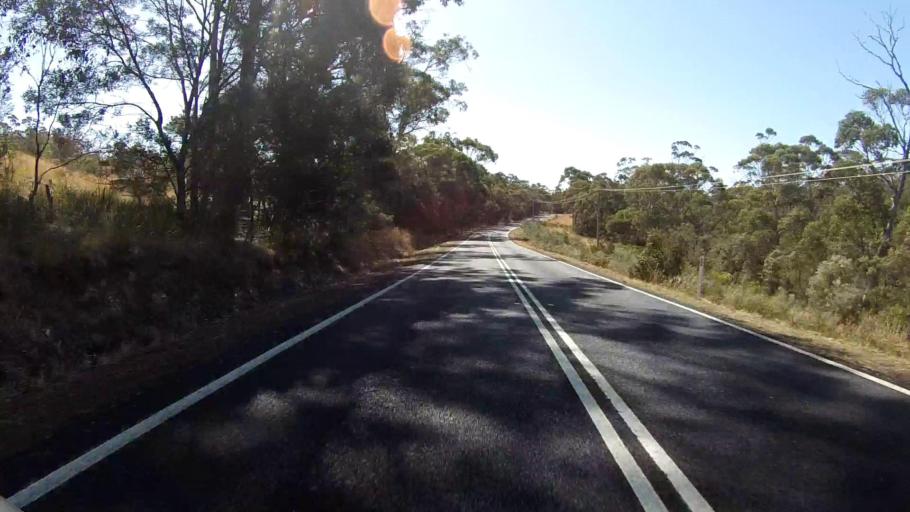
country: AU
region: Tasmania
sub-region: Sorell
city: Sorell
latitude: -42.4043
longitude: 147.9341
